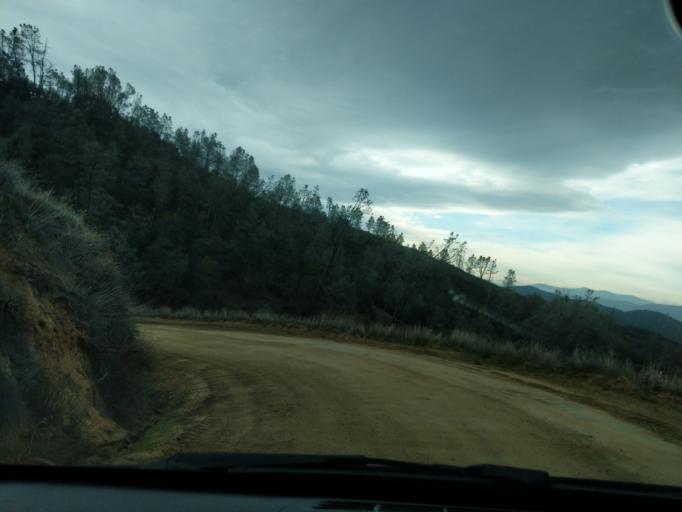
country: US
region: California
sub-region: Monterey County
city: Soledad
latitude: 36.5358
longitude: -121.3019
